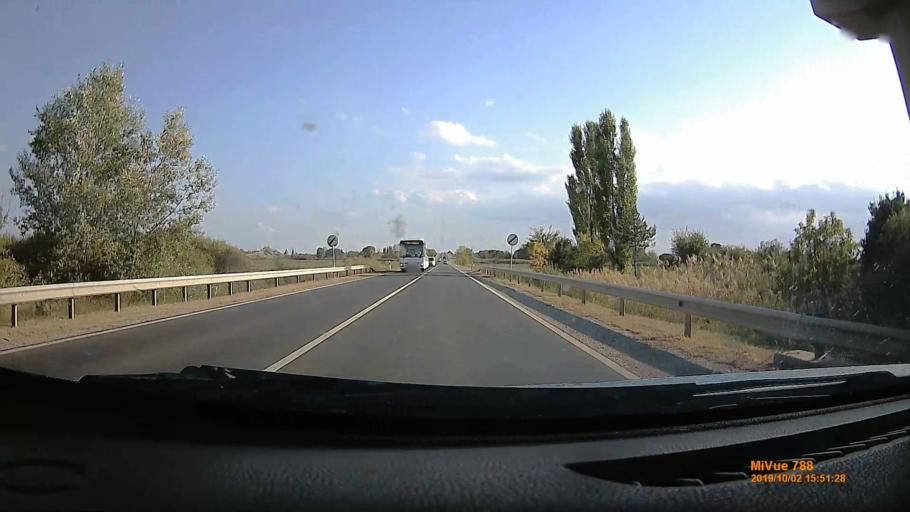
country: HU
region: Heves
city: Fuzesabony
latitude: 47.7560
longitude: 20.3950
